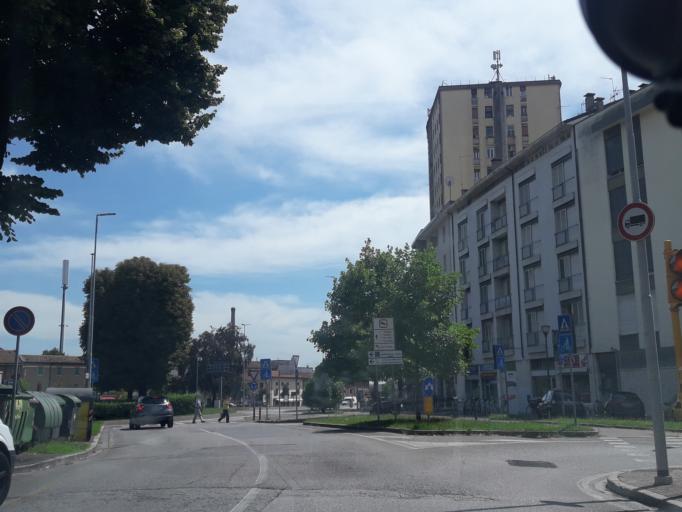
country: IT
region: Friuli Venezia Giulia
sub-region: Provincia di Udine
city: Udine
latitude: 46.0557
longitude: 13.2293
